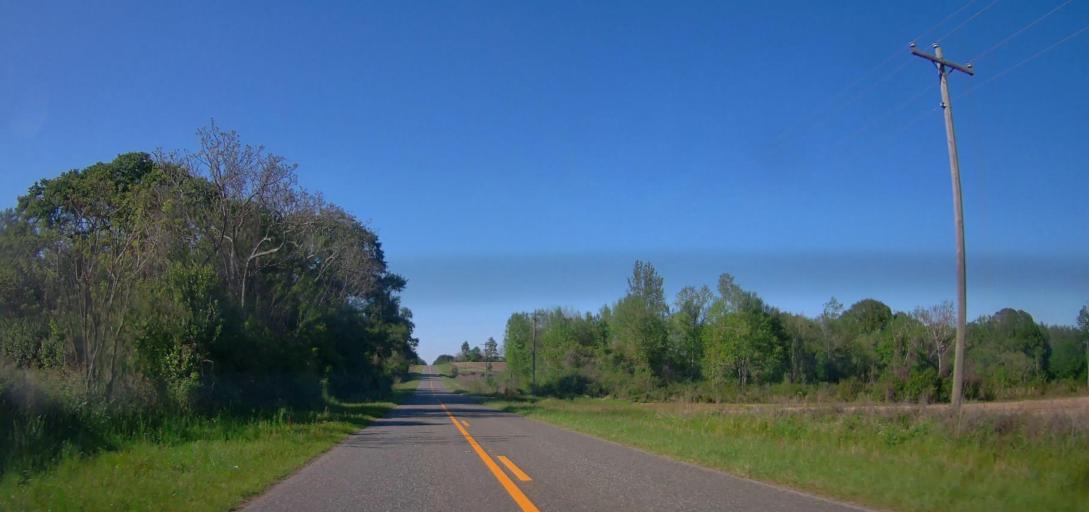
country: US
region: Georgia
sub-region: Turner County
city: Ashburn
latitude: 31.7718
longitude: -83.4896
